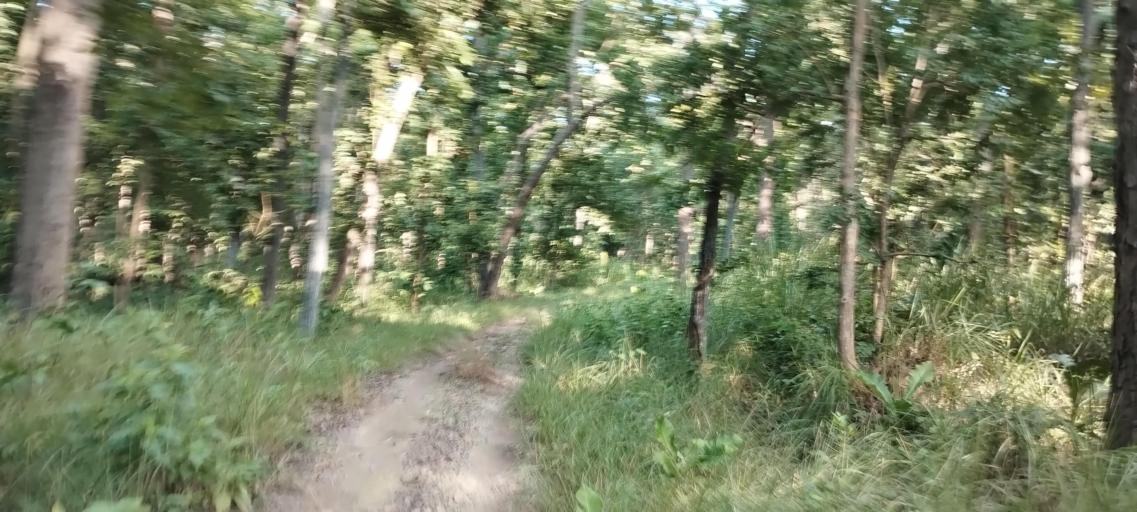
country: NP
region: Far Western
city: Tikapur
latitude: 28.5209
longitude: 81.2738
